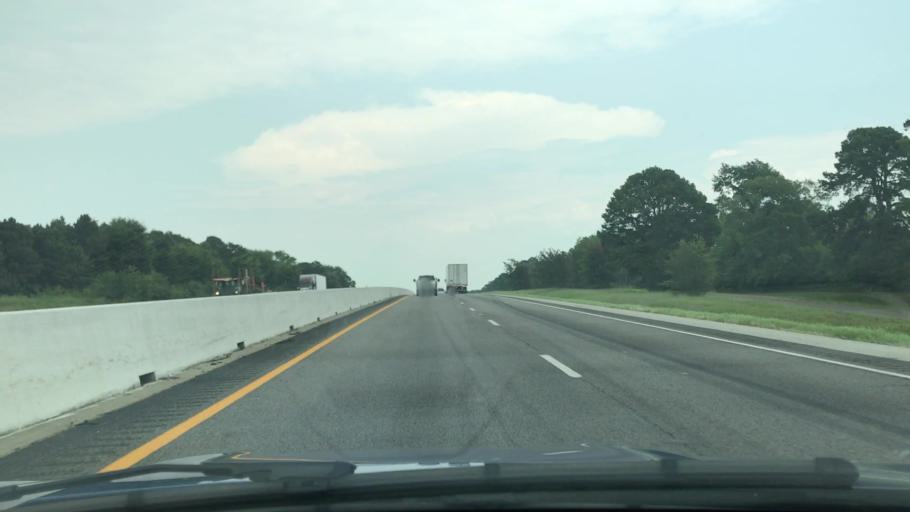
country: US
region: Texas
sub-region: Gregg County
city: Liberty City
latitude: 32.4376
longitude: -95.0244
